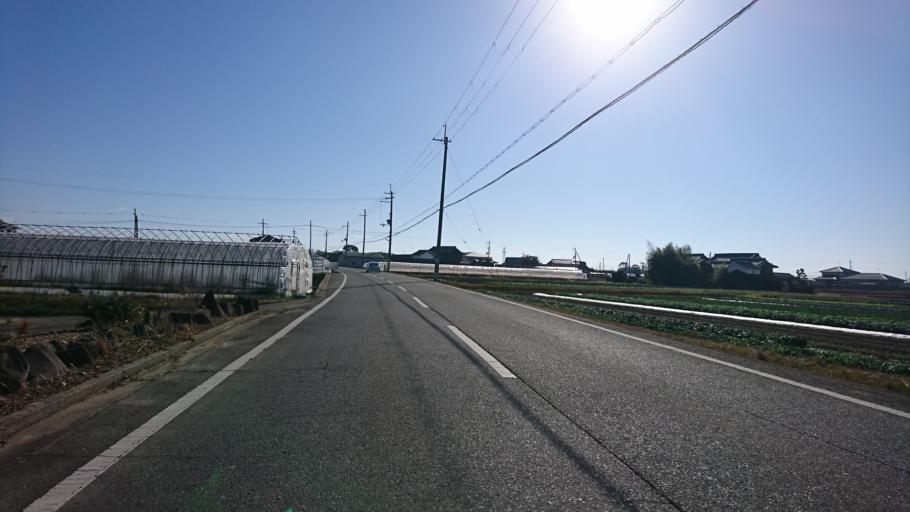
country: JP
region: Hyogo
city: Miki
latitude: 34.7279
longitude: 134.9536
